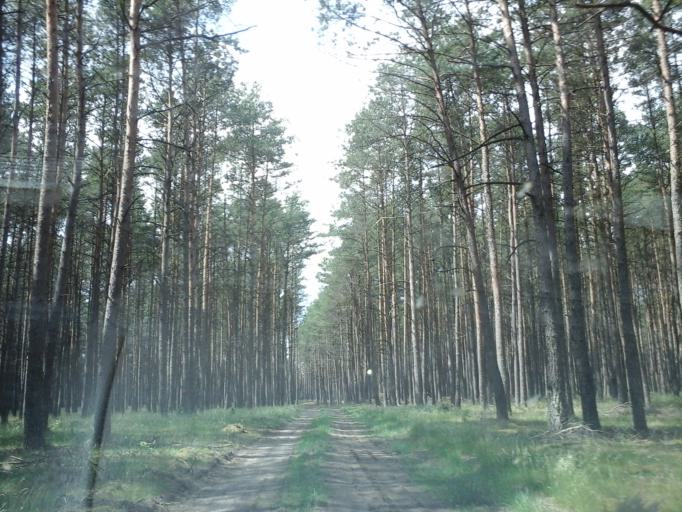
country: PL
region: West Pomeranian Voivodeship
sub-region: Powiat drawski
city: Kalisz Pomorski
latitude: 53.1878
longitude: 15.9046
